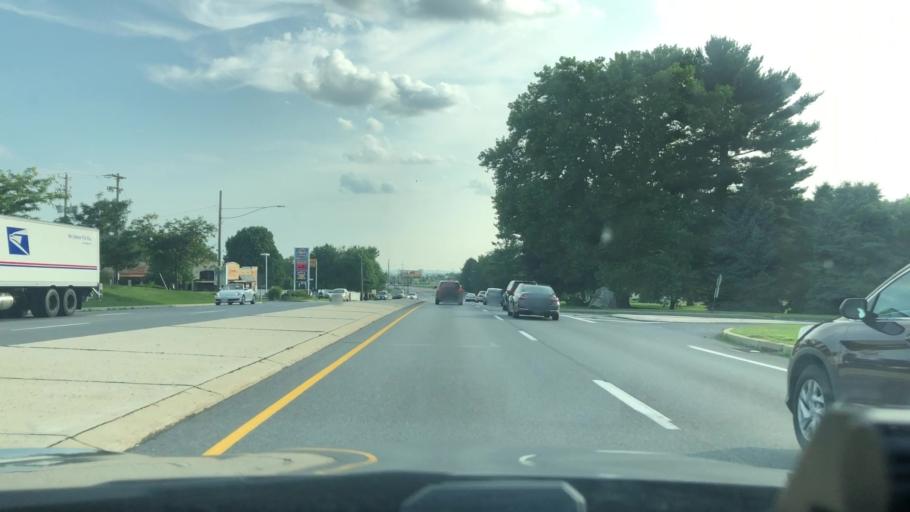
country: US
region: Pennsylvania
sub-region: Lehigh County
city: Fullerton
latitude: 40.6361
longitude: -75.4371
